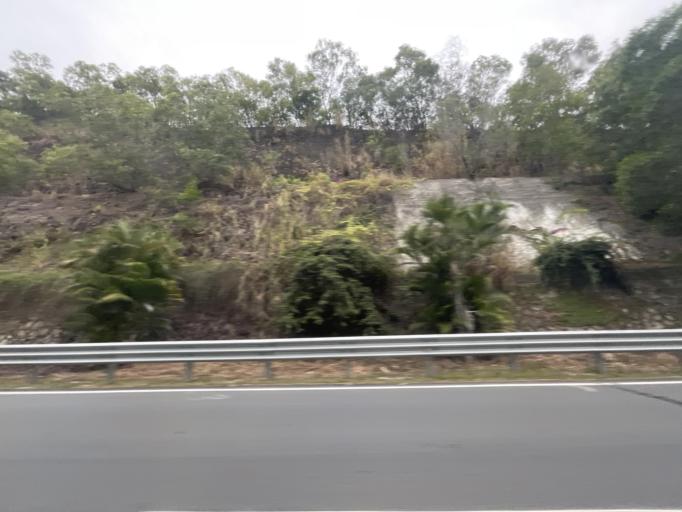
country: CN
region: Guangdong
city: Humen
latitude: 22.8074
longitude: 113.6434
